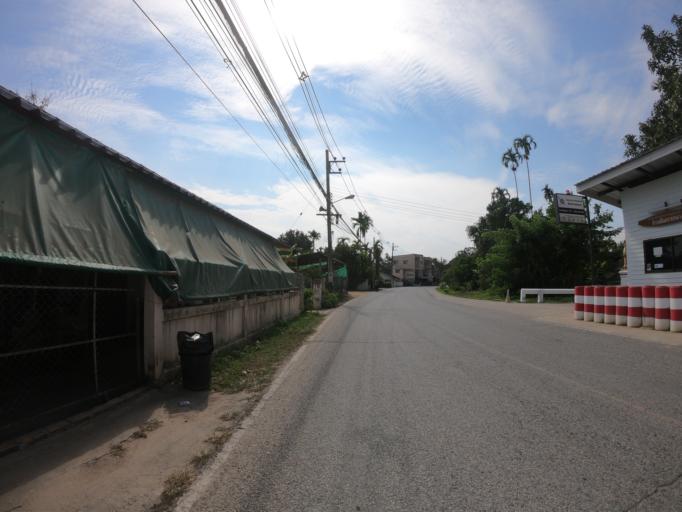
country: TH
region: Chiang Mai
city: San Sai
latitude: 18.8607
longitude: 99.0573
